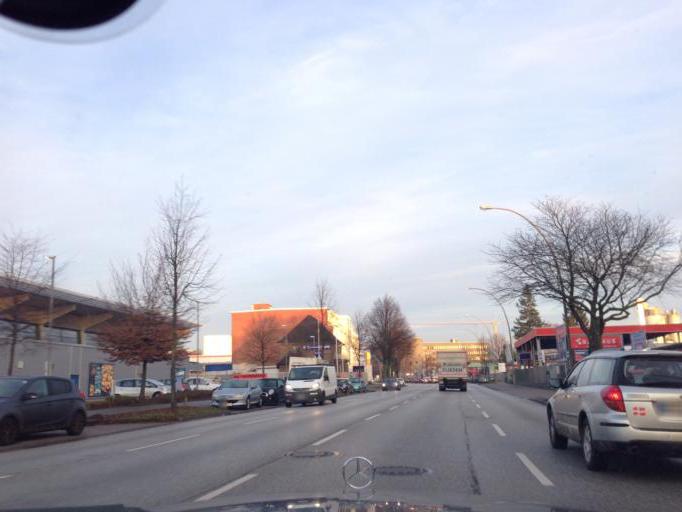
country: DE
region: Hamburg
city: Wandsbek
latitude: 53.5851
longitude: 10.1002
